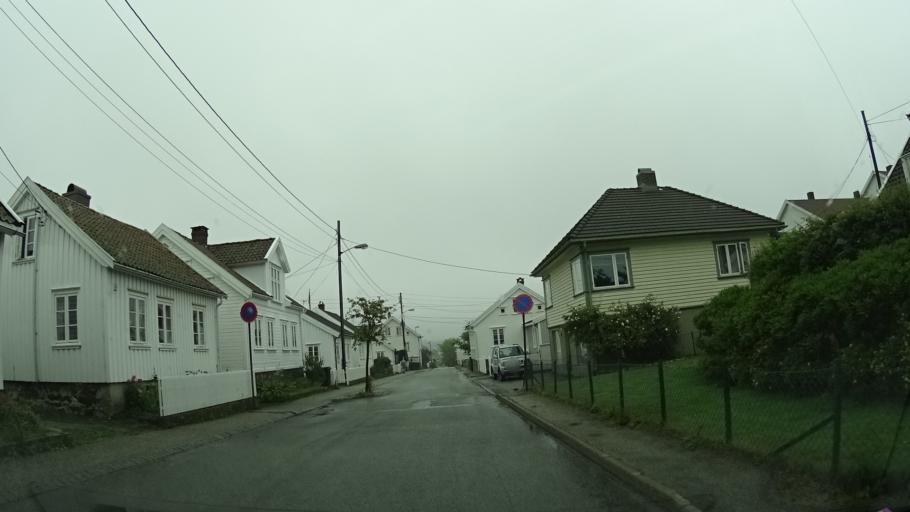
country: NO
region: Aust-Agder
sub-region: Lillesand
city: Lillesand
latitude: 58.2455
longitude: 8.3748
